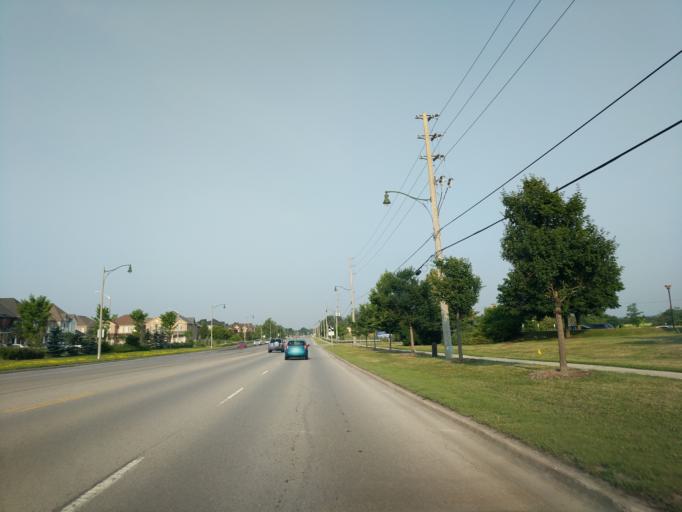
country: CA
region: Ontario
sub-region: York
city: Richmond Hill
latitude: 43.8963
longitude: -79.4058
